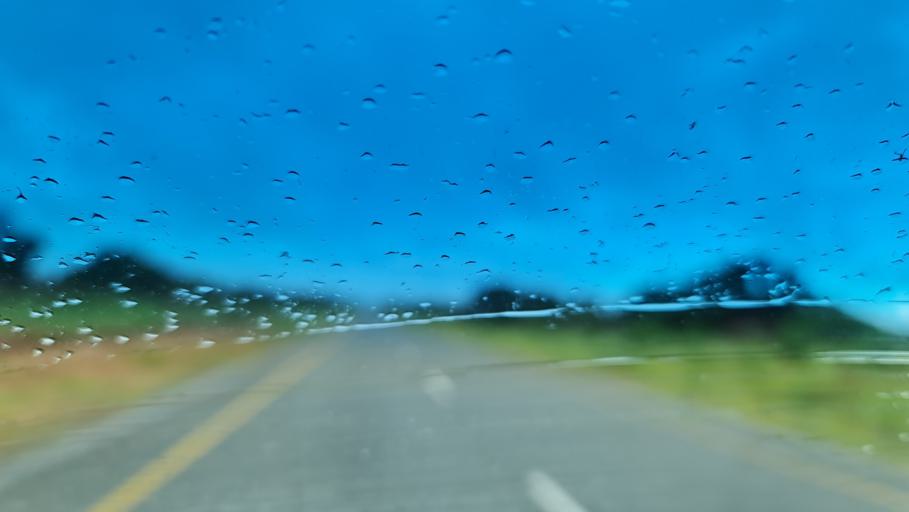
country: MZ
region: Nampula
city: Nampula
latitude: -15.5172
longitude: 39.3341
